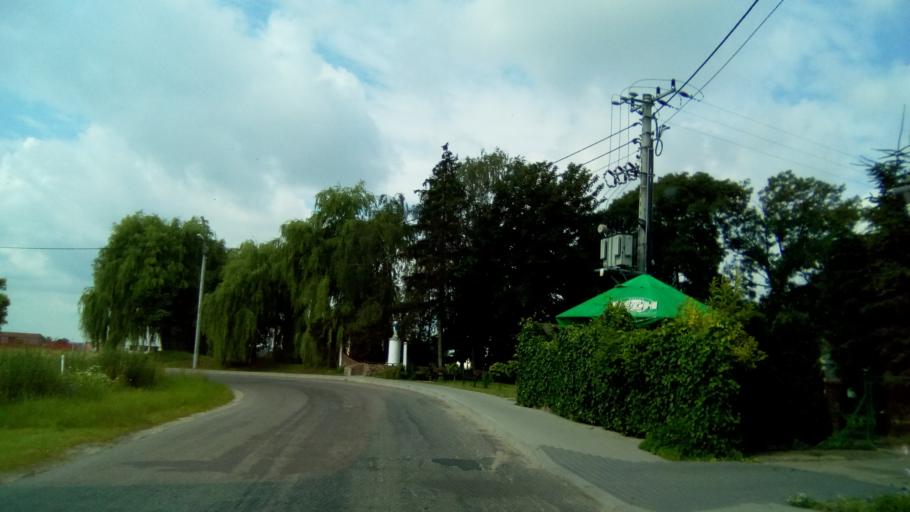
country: PL
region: Greater Poland Voivodeship
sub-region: Powiat gnieznienski
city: Czerniejewo
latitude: 52.4471
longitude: 17.5232
